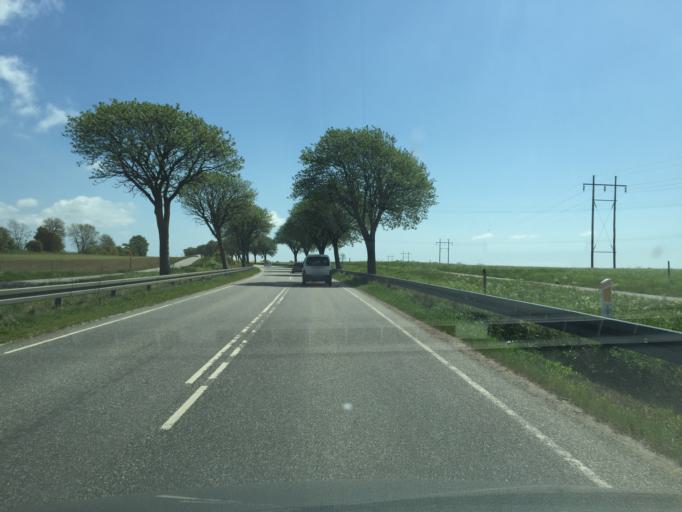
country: DK
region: Zealand
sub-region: Vordingborg Kommune
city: Stege
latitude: 54.9832
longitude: 12.1722
